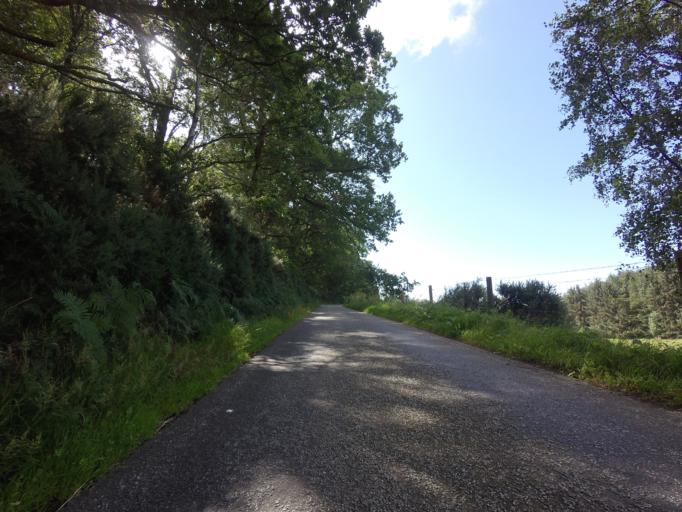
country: GB
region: Scotland
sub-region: Highland
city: Nairn
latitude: 57.5414
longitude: -3.8663
